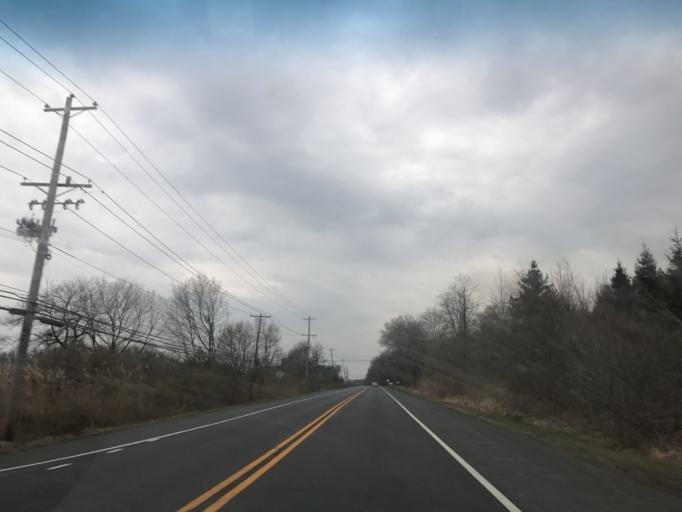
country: US
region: Delaware
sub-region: New Castle County
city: Glasgow
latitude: 39.6320
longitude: -75.7538
